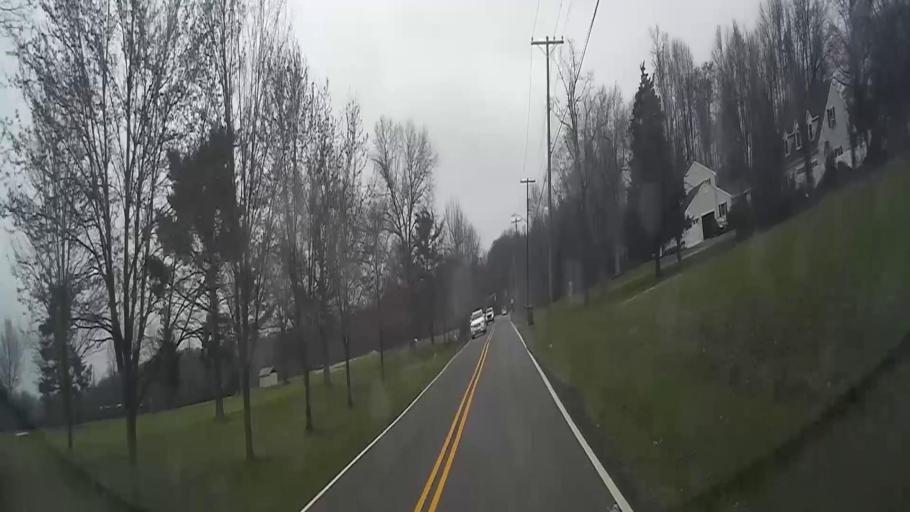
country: US
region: New Jersey
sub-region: Burlington County
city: Marlton
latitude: 39.8827
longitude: -74.8862
